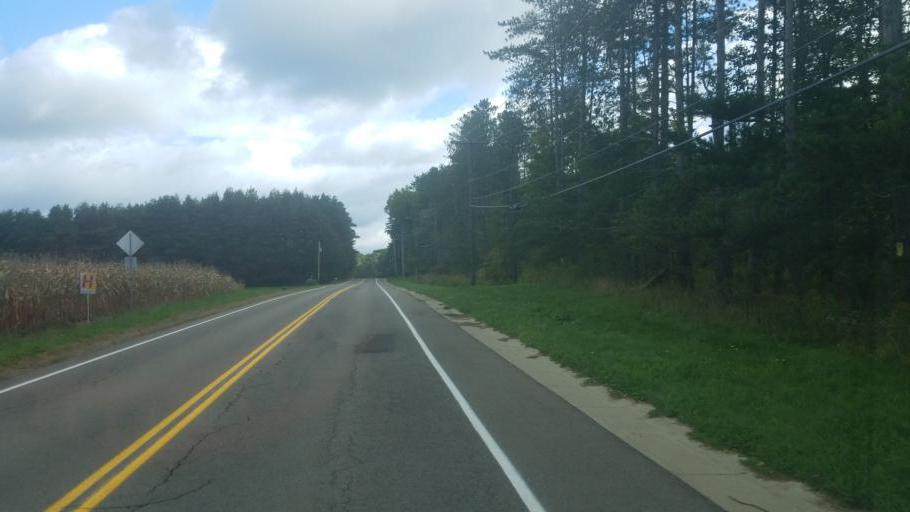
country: US
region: New York
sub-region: Cattaraugus County
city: Weston Mills
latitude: 42.0906
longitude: -78.3554
